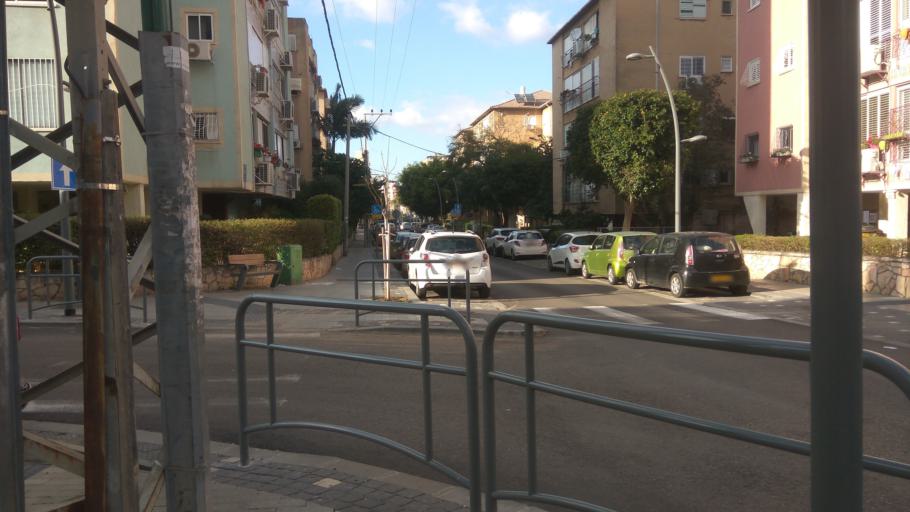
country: IL
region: Central District
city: Rishon LeZiyyon
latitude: 31.9670
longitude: 34.8063
